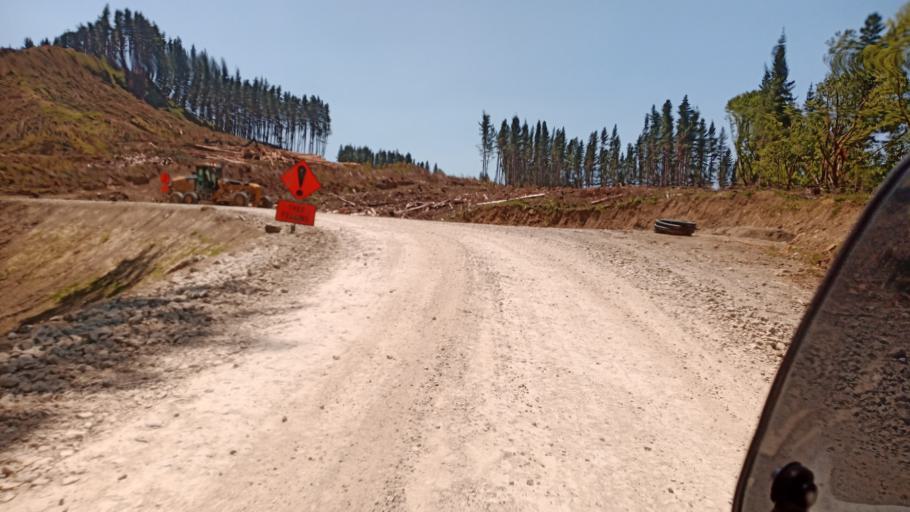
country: NZ
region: Gisborne
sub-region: Gisborne District
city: Gisborne
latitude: -38.2828
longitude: 177.9978
